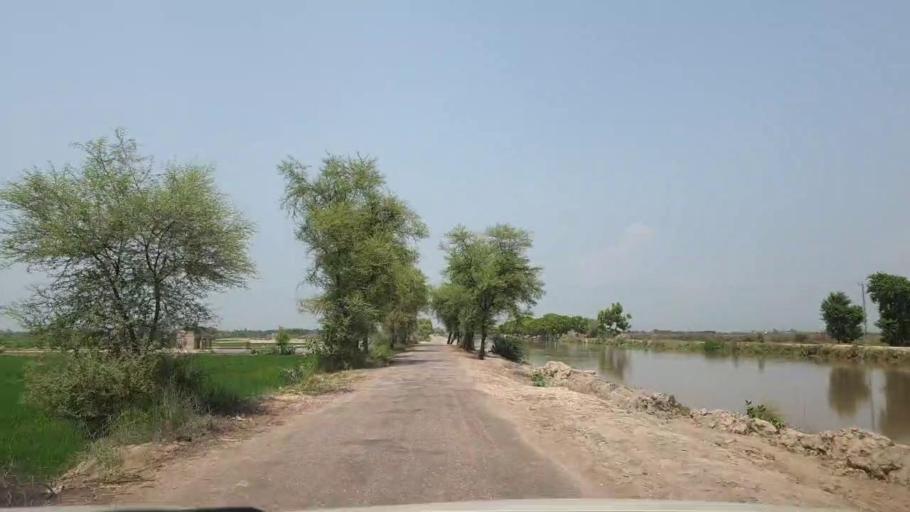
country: PK
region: Sindh
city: Dokri
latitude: 27.3449
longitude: 68.1115
